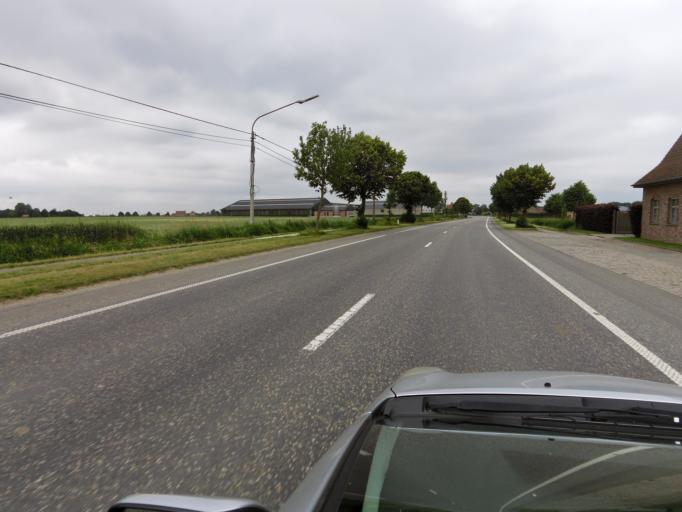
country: BE
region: Flanders
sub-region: Provincie West-Vlaanderen
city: Ieper
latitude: 50.8839
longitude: 2.8661
